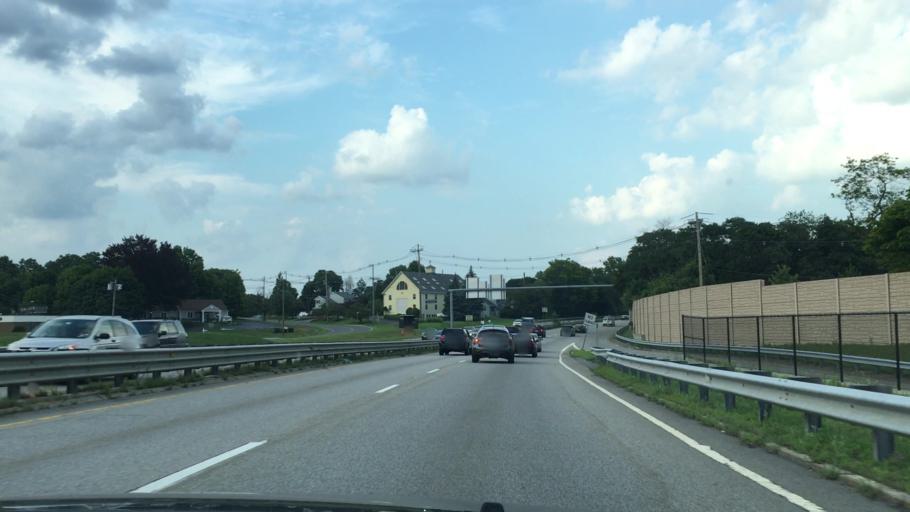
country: US
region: Massachusetts
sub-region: Essex County
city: Danvers
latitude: 42.5662
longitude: -70.9219
